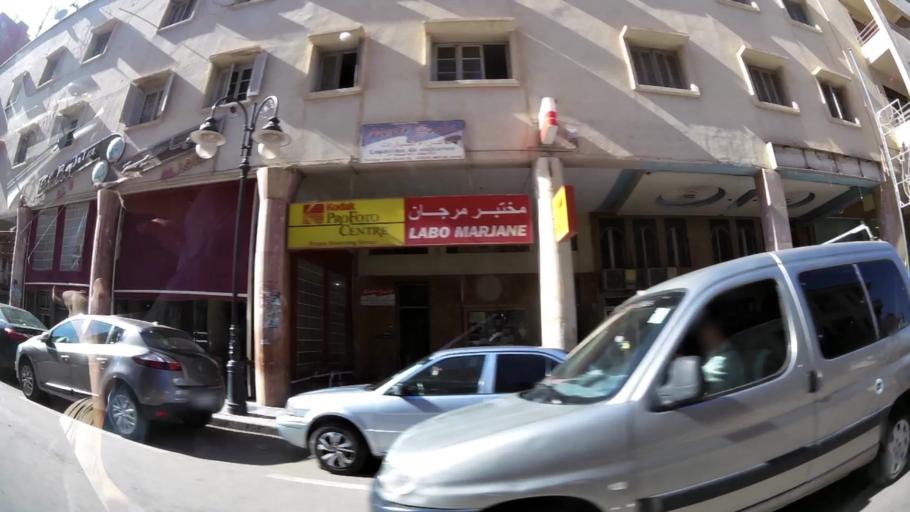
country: MA
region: Oriental
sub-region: Oujda-Angad
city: Oujda
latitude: 34.6807
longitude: -1.9183
